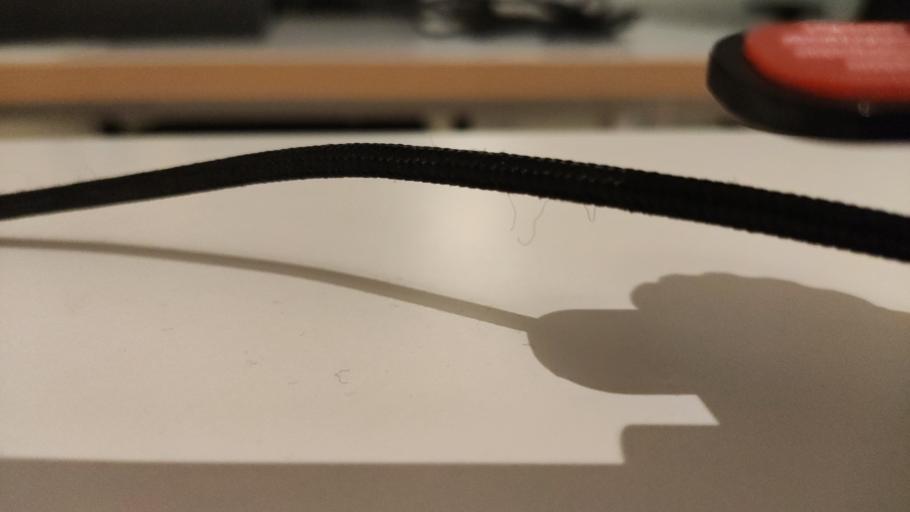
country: RU
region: Moskovskaya
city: Il'inskiy Pogost
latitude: 55.5119
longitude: 38.8714
